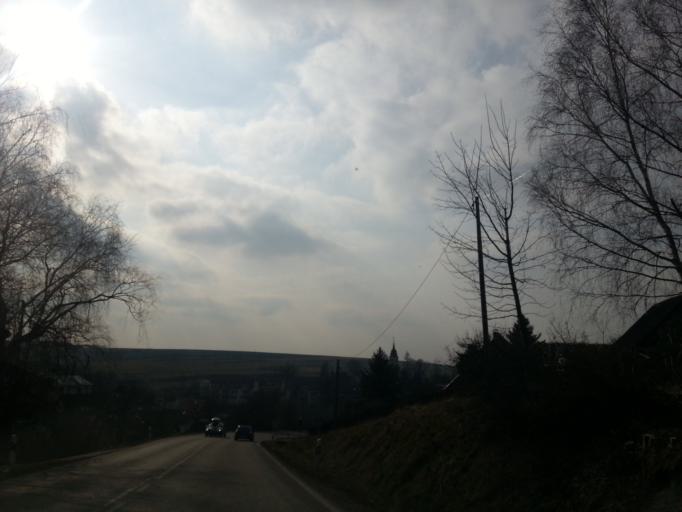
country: DE
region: Saxony
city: Wilsdruff
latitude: 51.0132
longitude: 13.4968
